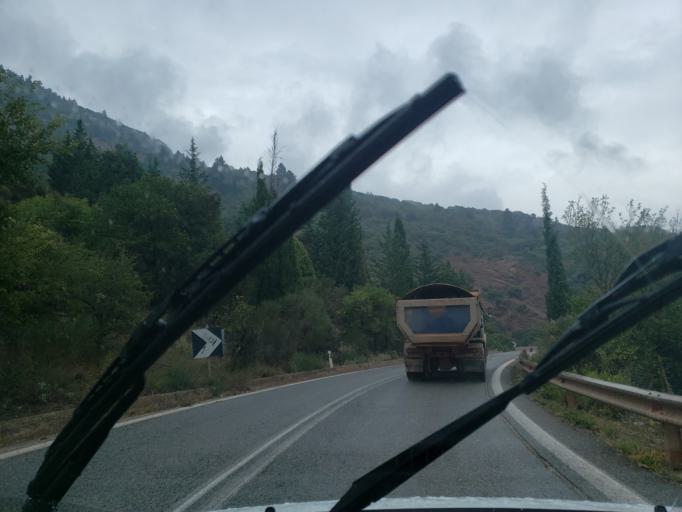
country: GR
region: Central Greece
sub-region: Nomos Fokidos
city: Amfissa
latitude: 38.5830
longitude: 22.3924
